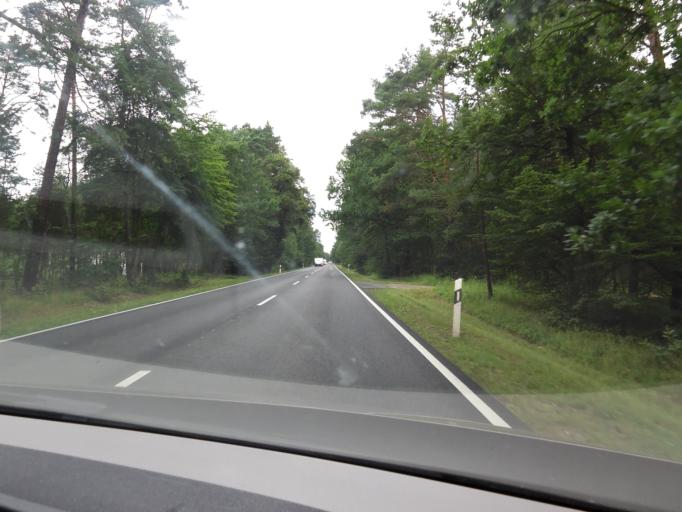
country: DE
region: Brandenburg
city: Furstenberg
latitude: 53.2024
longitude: 13.1346
